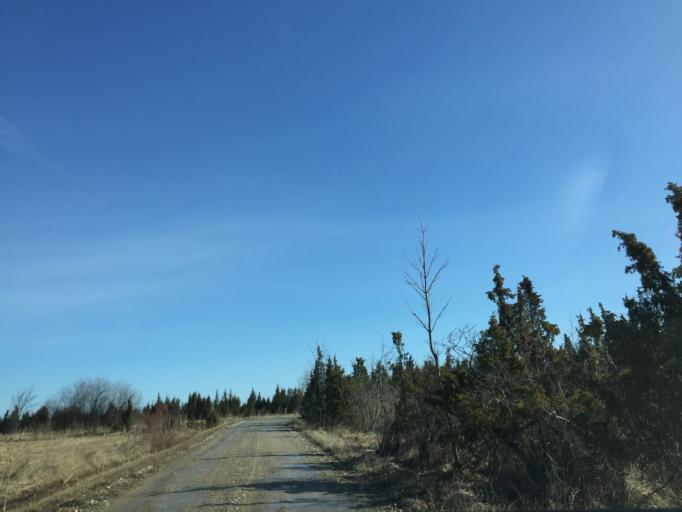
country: EE
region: Laeaene
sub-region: Haapsalu linn
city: Haapsalu
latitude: 58.6860
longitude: 23.5024
